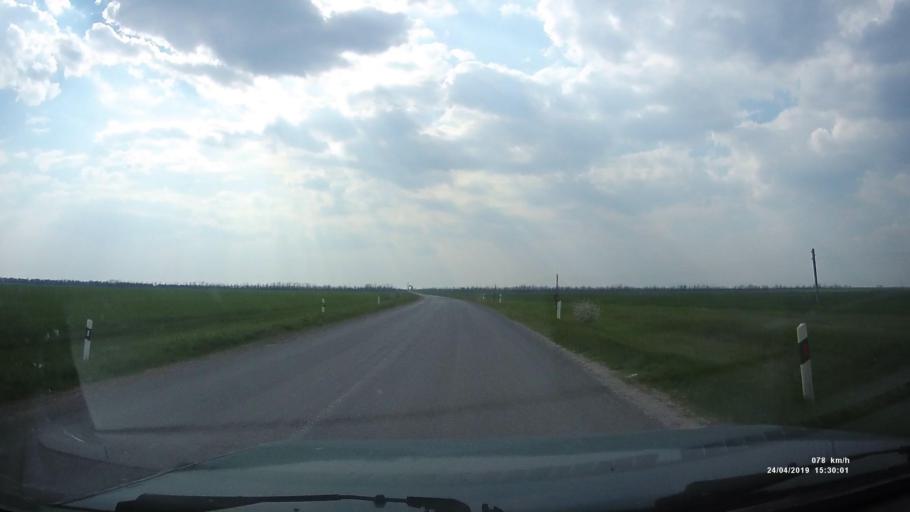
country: RU
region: Rostov
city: Remontnoye
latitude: 46.5998
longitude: 43.0145
